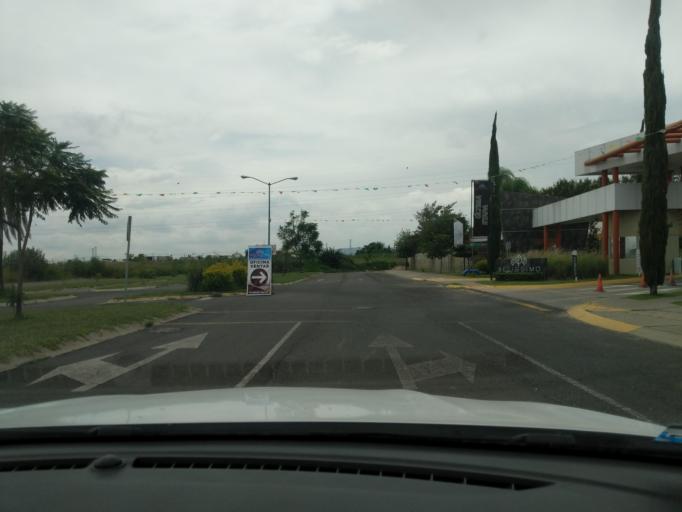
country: MX
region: Jalisco
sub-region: Zapopan
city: La Cuchilla (Extramuros de Tesistan)
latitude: 20.7790
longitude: -103.4637
